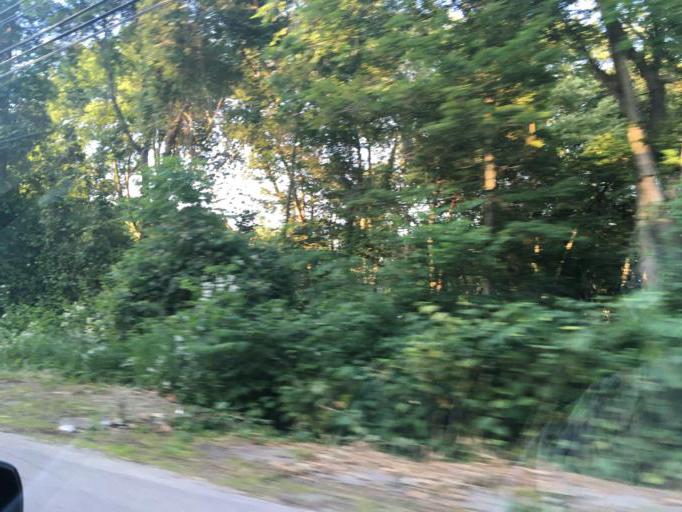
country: US
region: Rhode Island
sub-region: Kent County
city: East Greenwich
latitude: 41.6384
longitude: -71.4946
